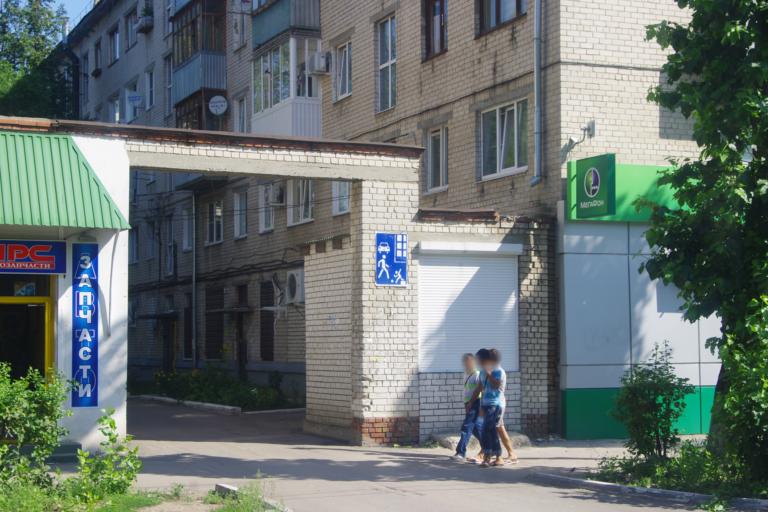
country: RU
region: Samara
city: Tol'yatti
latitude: 53.5083
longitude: 49.4157
